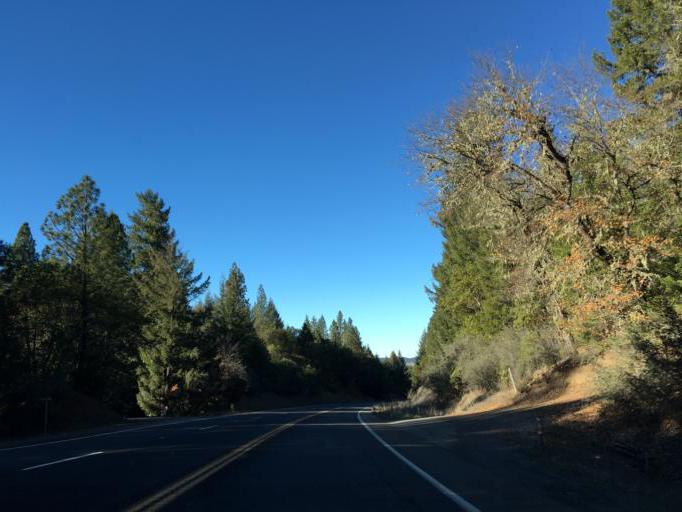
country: US
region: California
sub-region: Mendocino County
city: Laytonville
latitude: 39.7155
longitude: -123.4986
